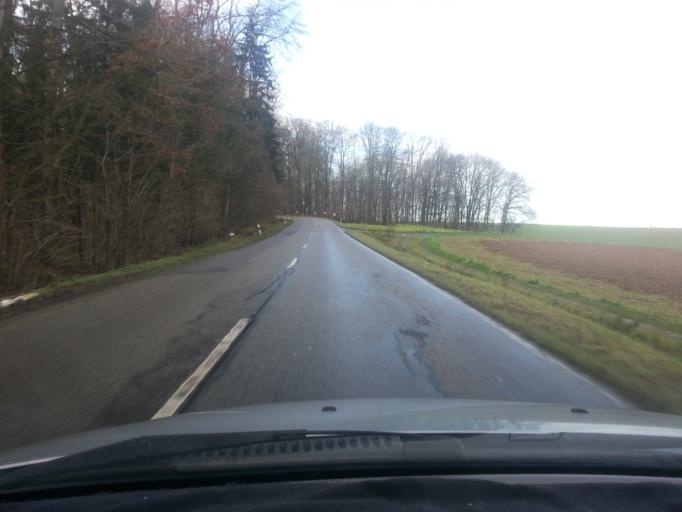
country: DE
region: Baden-Wuerttemberg
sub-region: Regierungsbezirk Stuttgart
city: Eppingen
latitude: 49.1609
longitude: 8.8743
